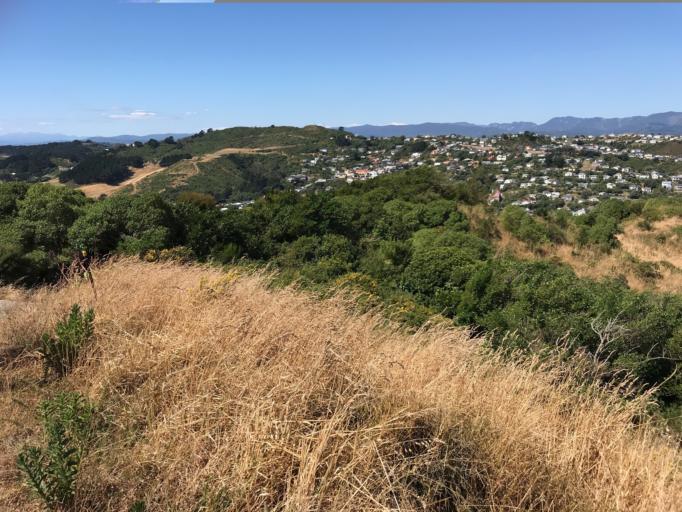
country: NZ
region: Wellington
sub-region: Wellington City
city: Brooklyn
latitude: -41.3337
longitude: 174.7665
